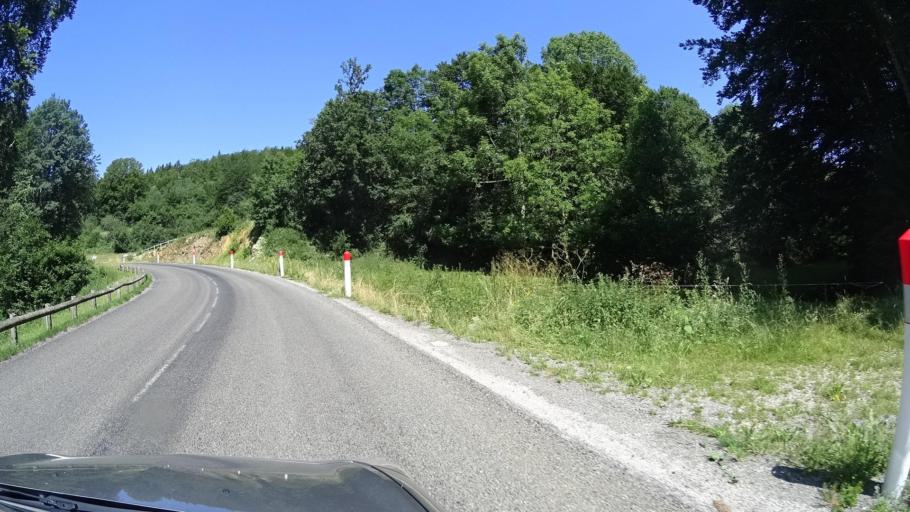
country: FR
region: Franche-Comte
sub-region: Departement du Jura
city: Longchaumois
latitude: 46.5050
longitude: 5.9452
